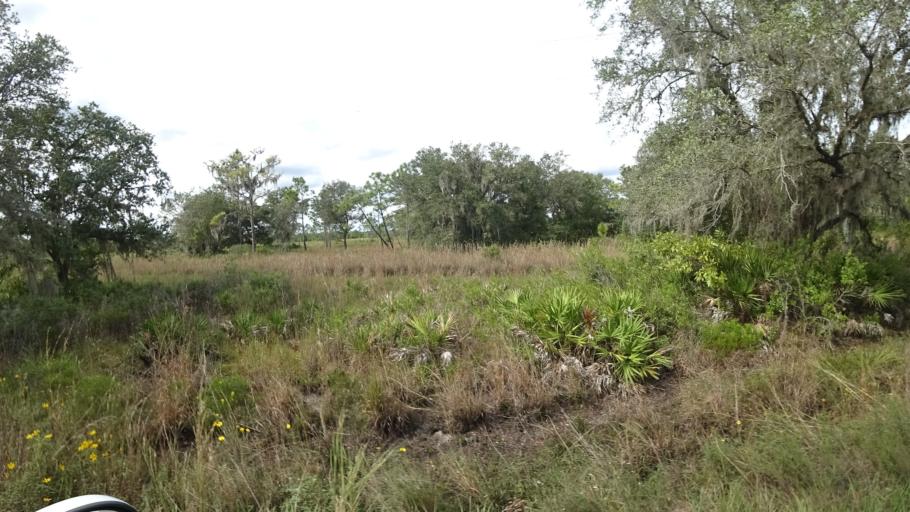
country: US
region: Florida
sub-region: Hillsborough County
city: Wimauma
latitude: 27.5374
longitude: -82.1454
